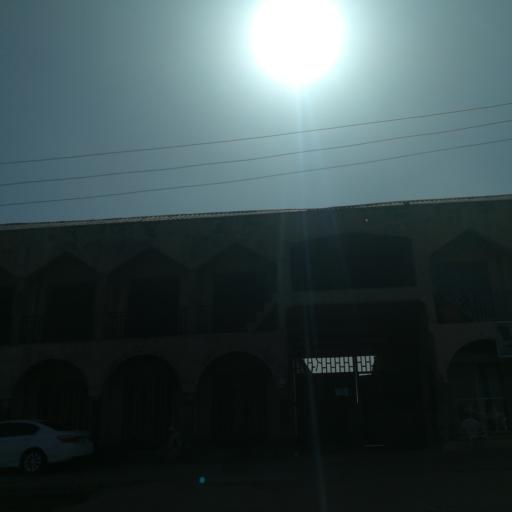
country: NG
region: Kano
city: Kano
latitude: 12.0113
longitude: 8.5221
